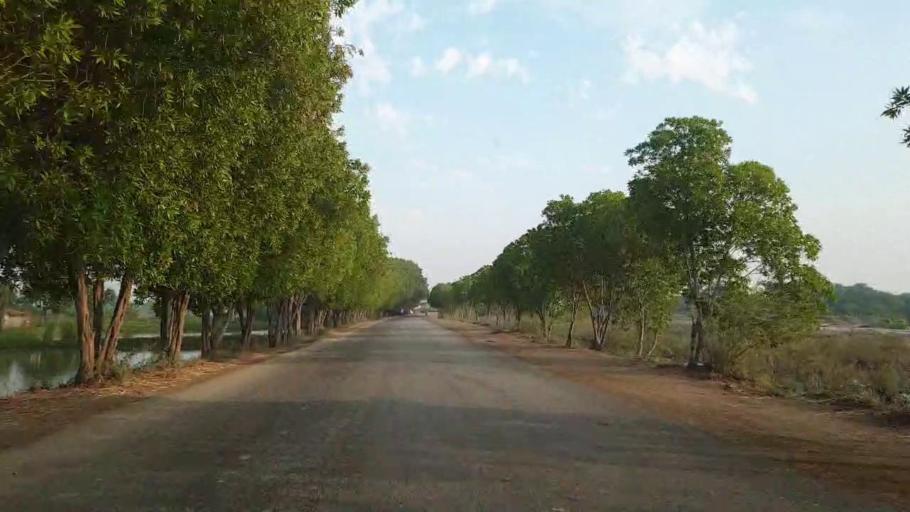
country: PK
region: Sindh
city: Tando Bago
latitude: 24.7176
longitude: 68.9398
